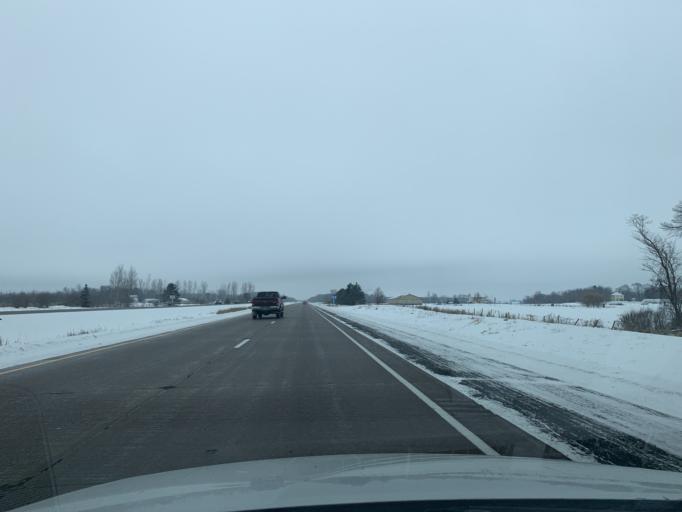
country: US
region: Minnesota
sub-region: Chisago County
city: Rush City
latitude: 45.6399
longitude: -92.9921
